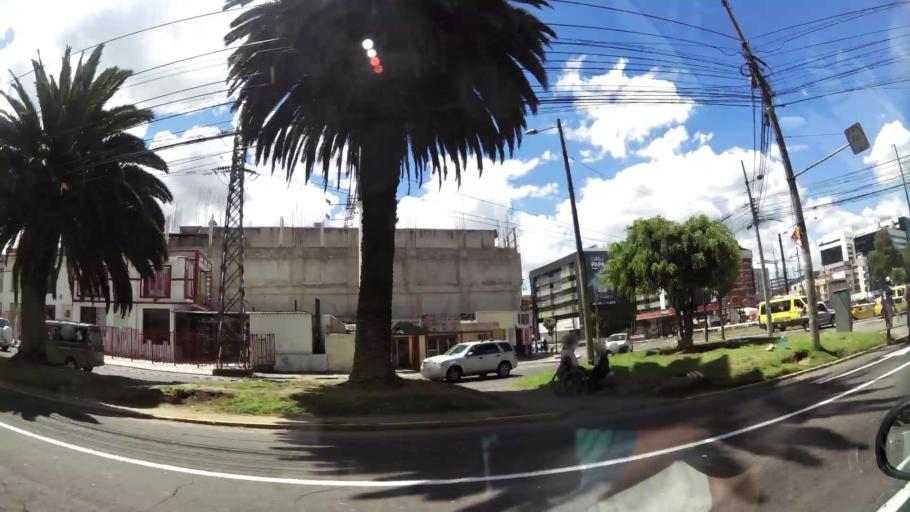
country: EC
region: Pichincha
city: Quito
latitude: -0.1755
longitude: -78.4889
